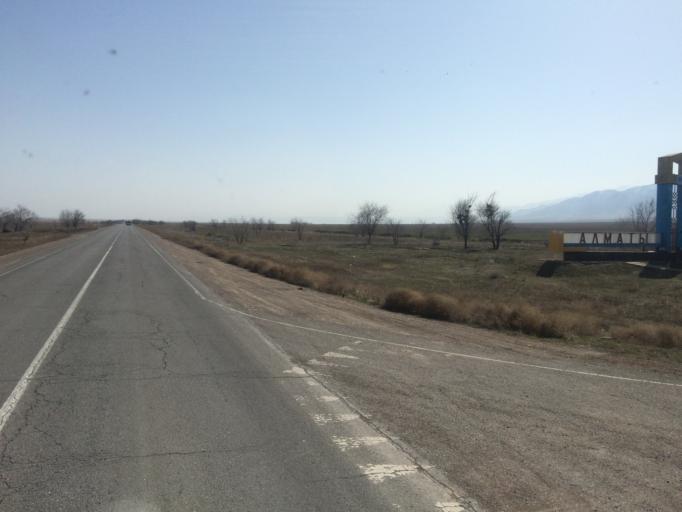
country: KG
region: Chuy
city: Ivanovka
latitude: 43.3708
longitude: 75.2949
